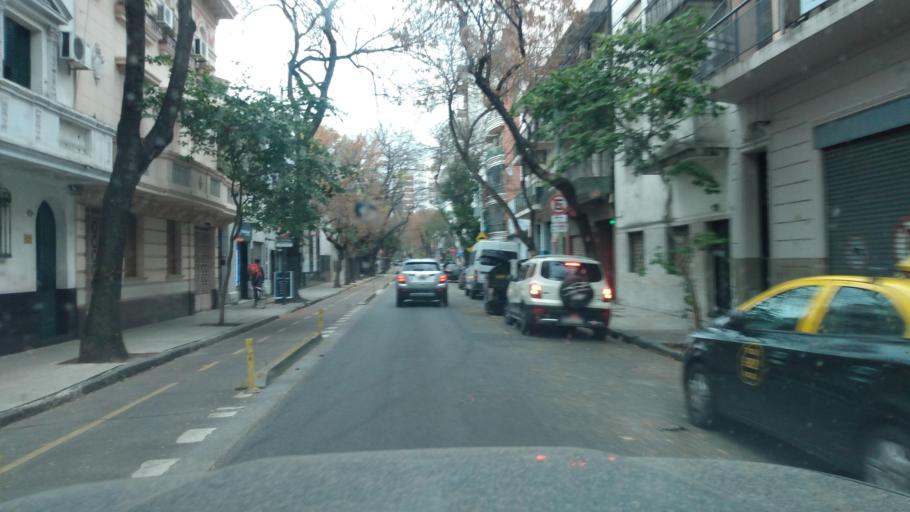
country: AR
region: Buenos Aires F.D.
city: Buenos Aires
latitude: -34.6197
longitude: -58.3959
